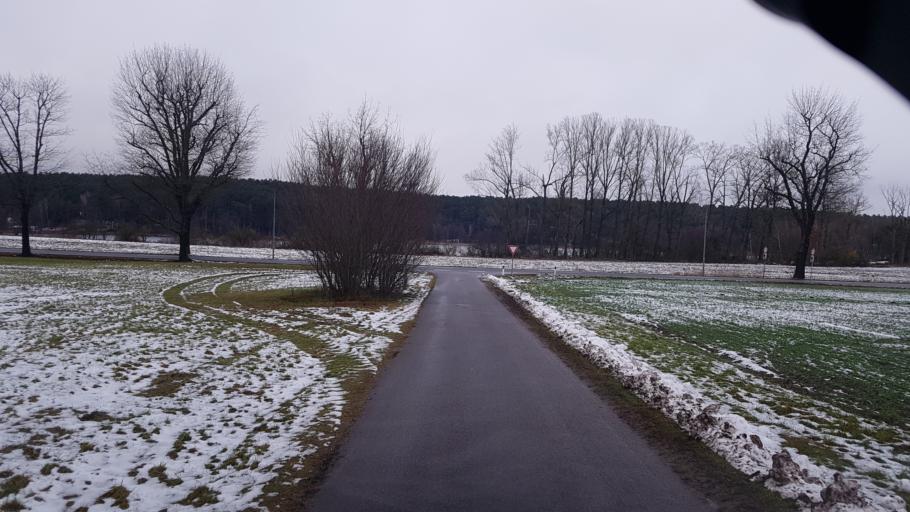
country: DE
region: Brandenburg
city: Schenkendobern
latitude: 51.9690
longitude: 14.5768
